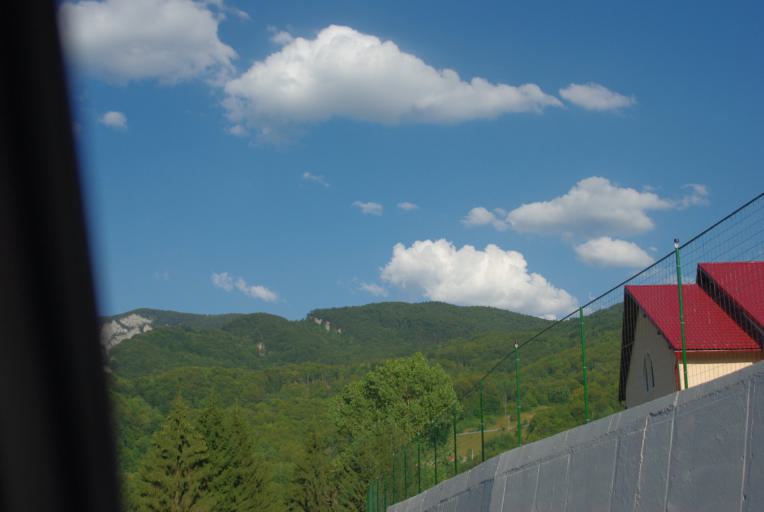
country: RO
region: Bihor
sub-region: Comuna Pietroasa
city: Pietroasa
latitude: 46.6007
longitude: 22.6448
